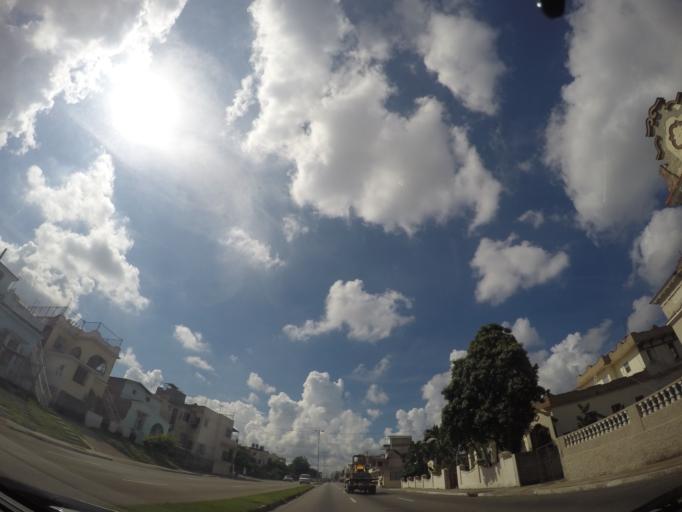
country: CU
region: La Habana
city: Cerro
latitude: 23.0987
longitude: -82.4211
